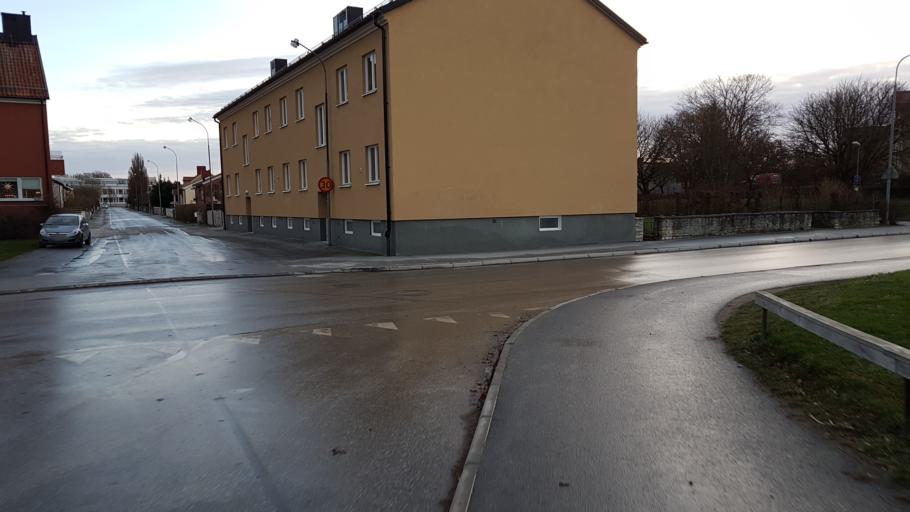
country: SE
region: Gotland
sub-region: Gotland
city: Visby
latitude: 57.6285
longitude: 18.2898
